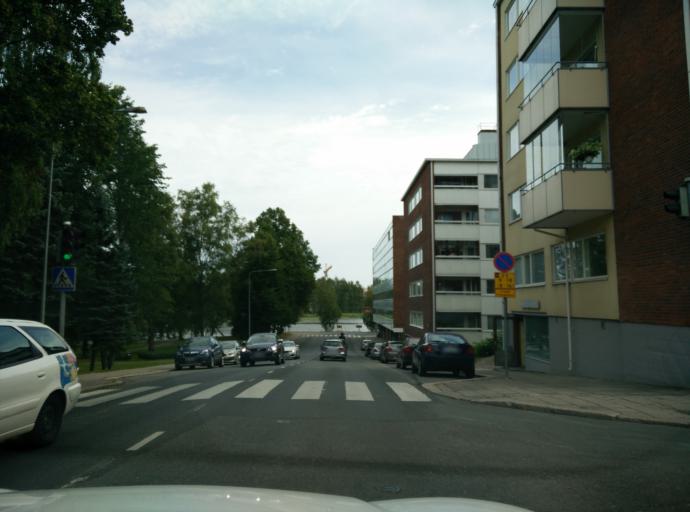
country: FI
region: Haeme
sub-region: Haemeenlinna
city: Haemeenlinna
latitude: 60.9994
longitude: 24.4668
